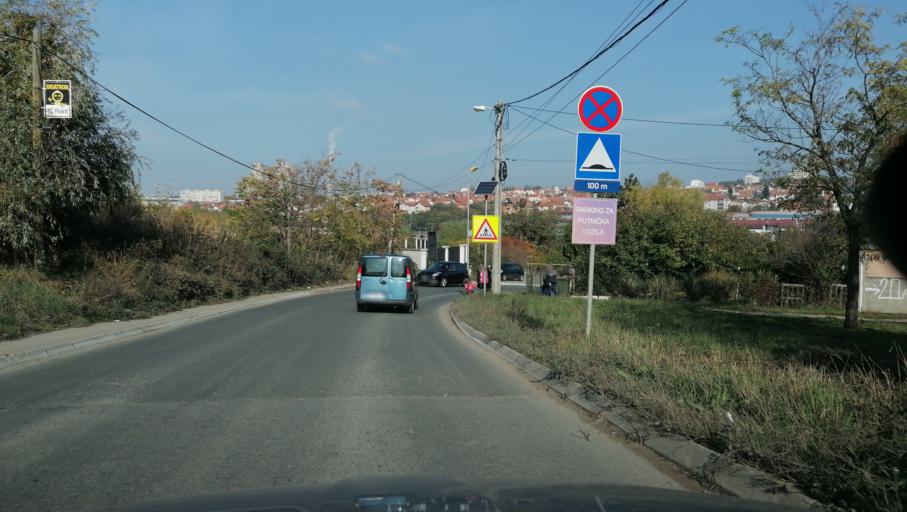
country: RS
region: Central Serbia
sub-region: Belgrade
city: Zvezdara
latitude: 44.7708
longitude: 20.5171
